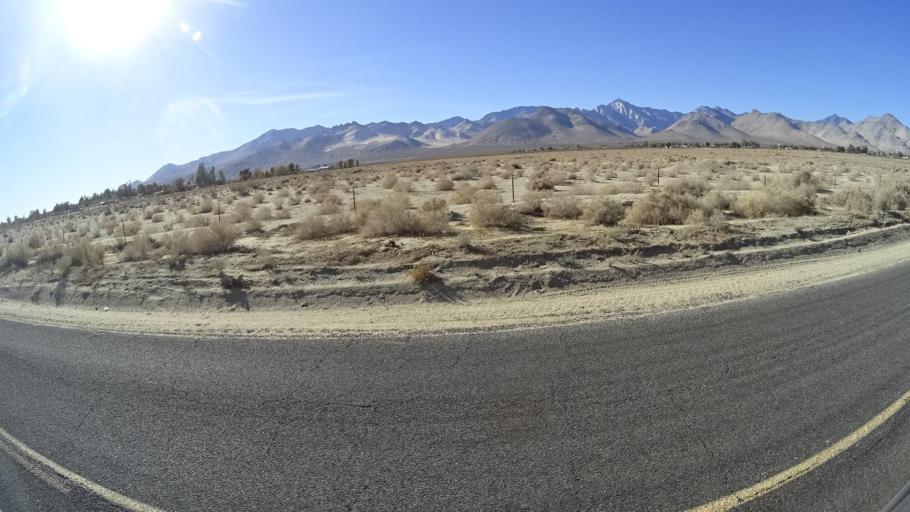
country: US
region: California
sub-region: Kern County
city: Inyokern
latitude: 35.7193
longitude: -117.8331
